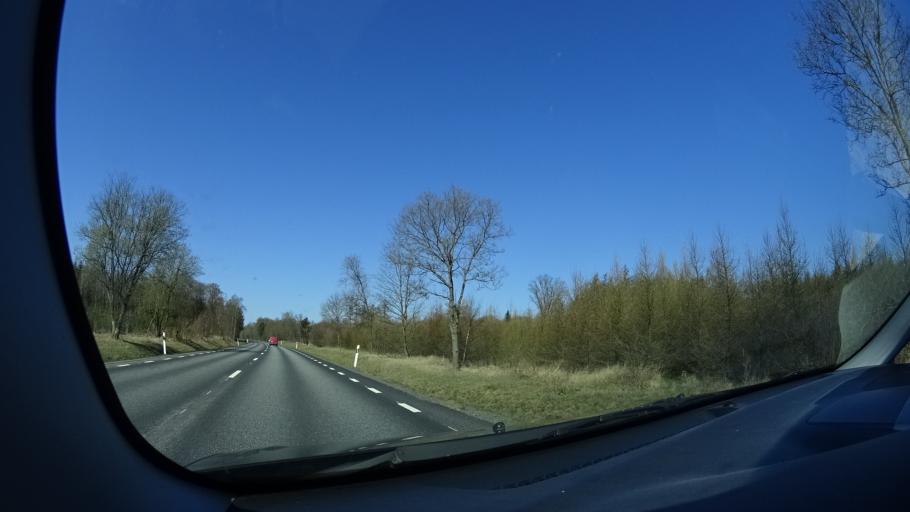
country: SE
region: Skane
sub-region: Angelholms Kommun
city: Strovelstorp
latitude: 56.2002
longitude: 12.8233
